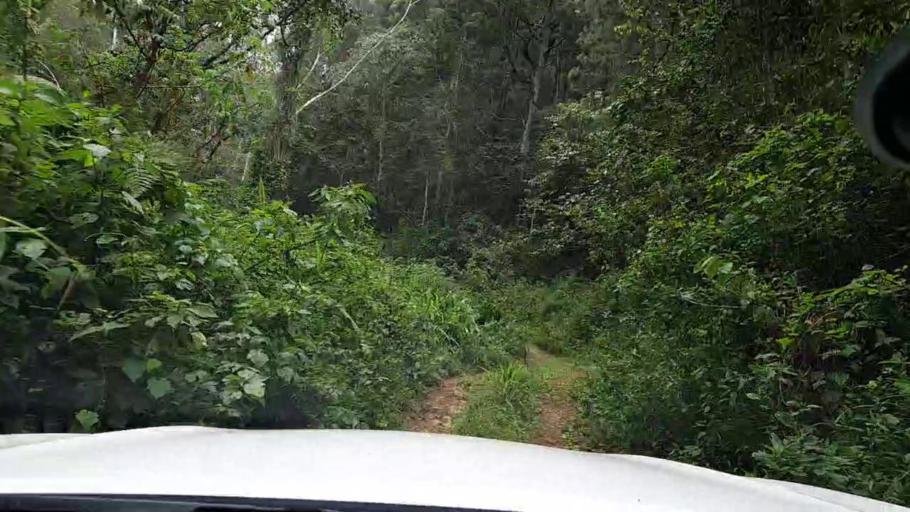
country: RW
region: Western Province
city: Kibuye
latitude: -2.2892
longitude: 29.3056
